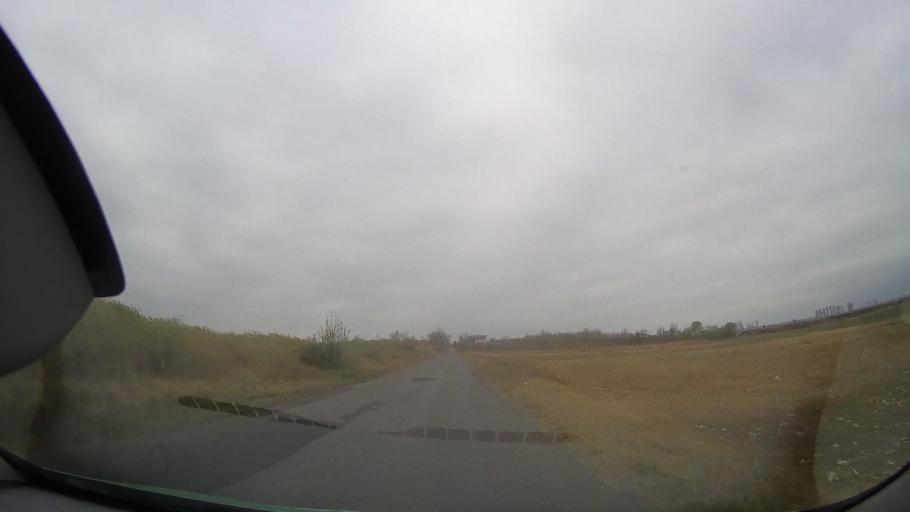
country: RO
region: Buzau
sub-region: Comuna Luciu
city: Luciu
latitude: 44.9795
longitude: 27.0458
